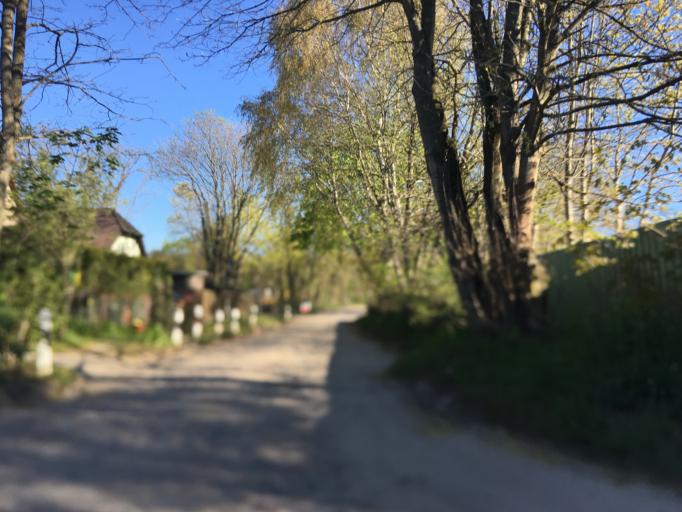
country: DE
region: Brandenburg
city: Bernau bei Berlin
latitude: 52.6930
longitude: 13.5489
